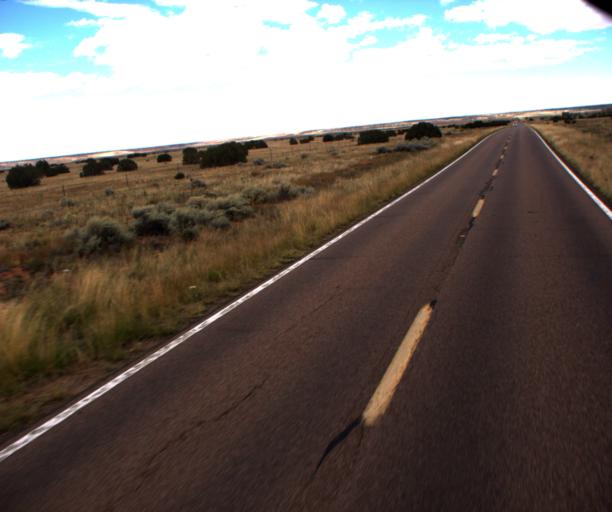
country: US
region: Arizona
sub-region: Navajo County
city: Heber-Overgaard
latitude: 34.5966
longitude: -110.3913
